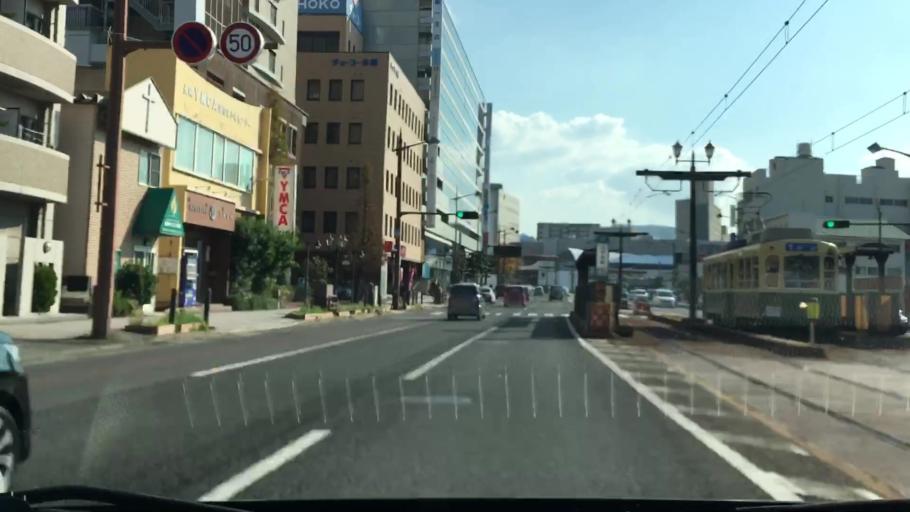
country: JP
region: Nagasaki
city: Nagasaki-shi
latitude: 32.7557
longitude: 129.8702
